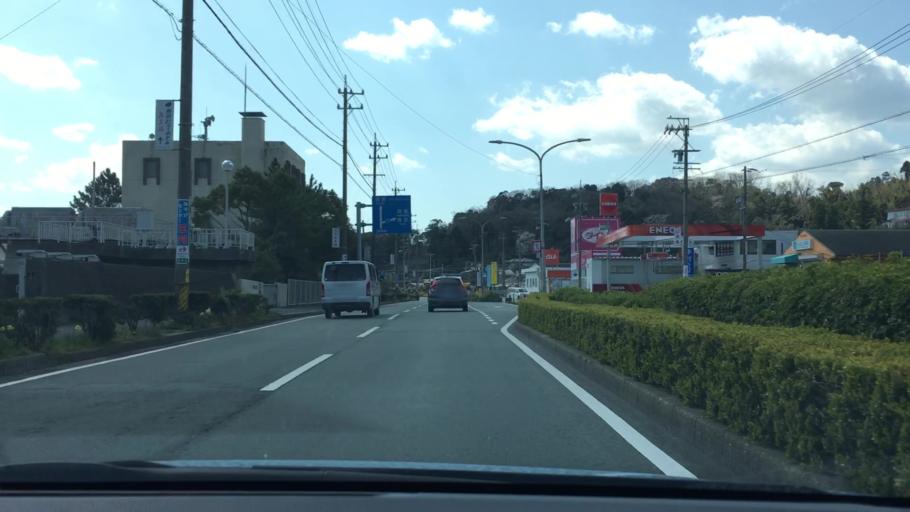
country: JP
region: Mie
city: Toba
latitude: 34.4761
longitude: 136.8456
